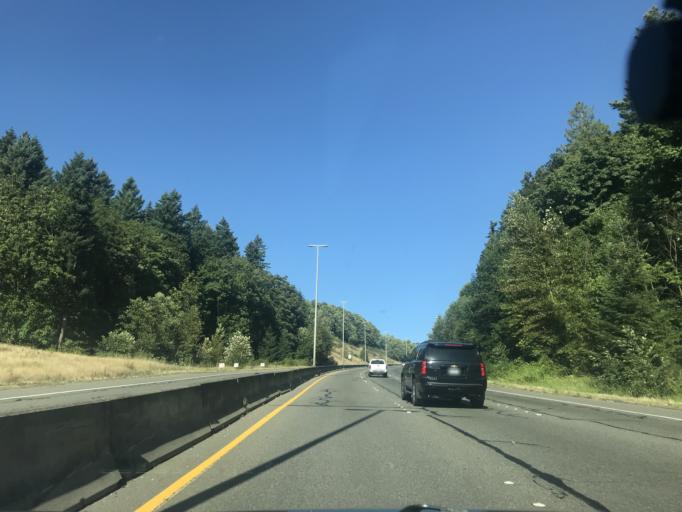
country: US
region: Washington
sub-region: King County
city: Lea Hill
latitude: 47.3550
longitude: -122.2055
